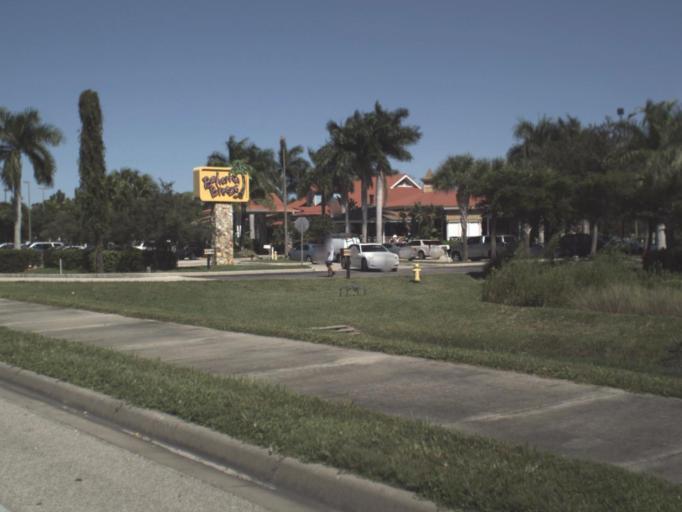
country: US
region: Florida
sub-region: Lee County
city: Villas
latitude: 26.5284
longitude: -81.8711
